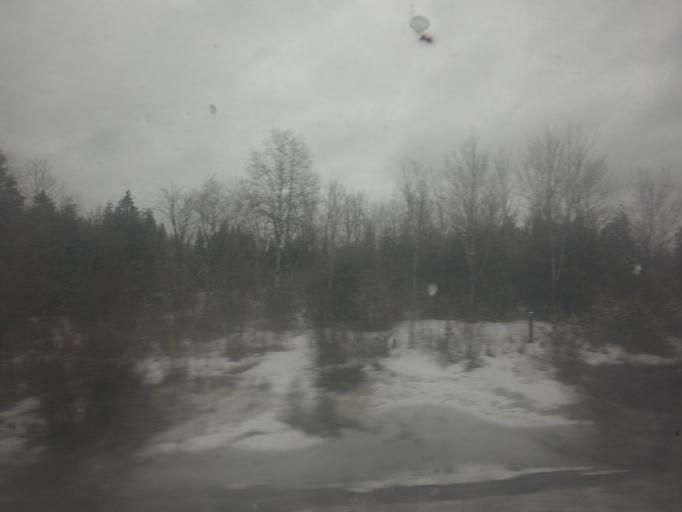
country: CA
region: Ontario
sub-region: Lanark County
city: Smiths Falls
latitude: 45.0115
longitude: -75.9523
